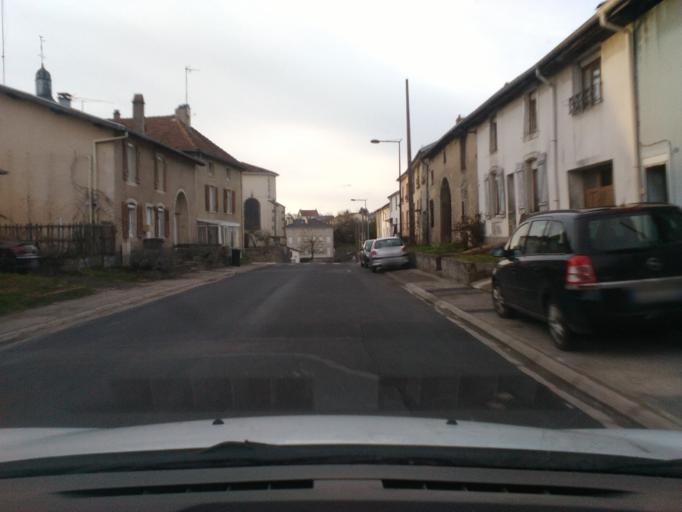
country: FR
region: Lorraine
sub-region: Departement des Vosges
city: Charmes
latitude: 48.3683
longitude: 6.3174
